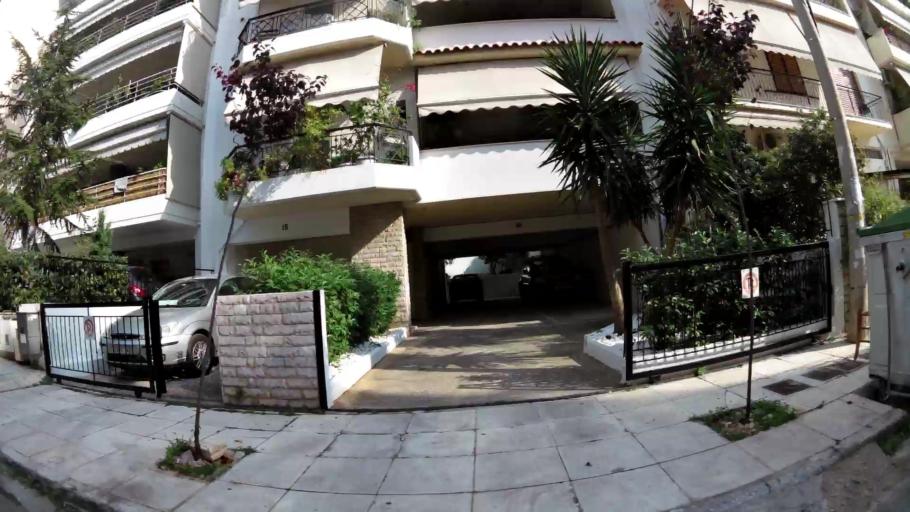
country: GR
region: Attica
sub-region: Nomarchia Athinas
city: Nea Smyrni
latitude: 37.9366
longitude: 23.7139
